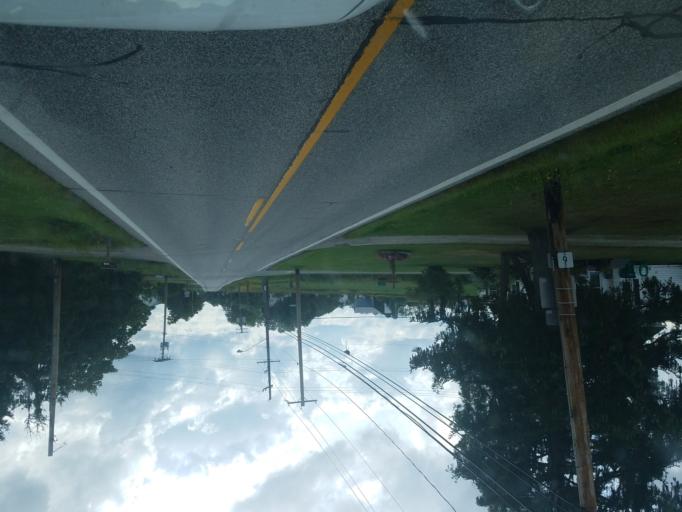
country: US
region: Ohio
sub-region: Geauga County
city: Burton
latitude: 41.4340
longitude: -81.1417
